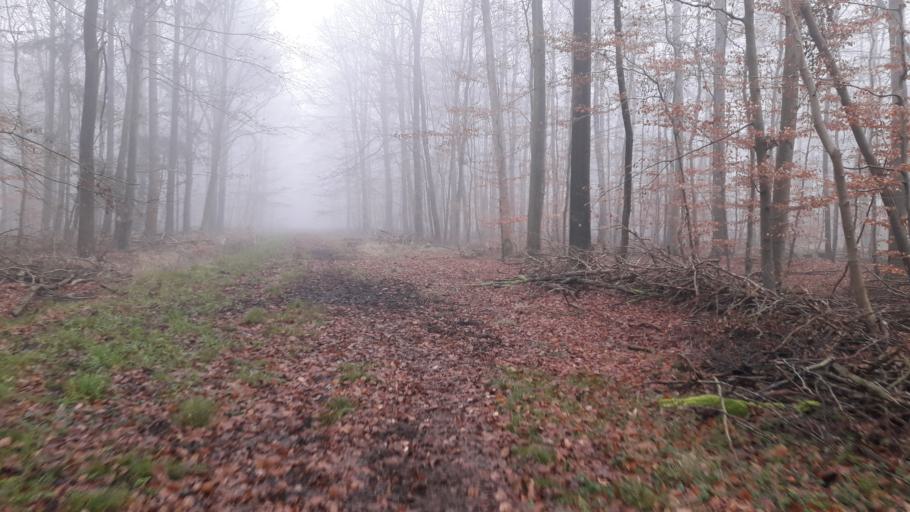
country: DE
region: Schleswig-Holstein
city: Quickborn
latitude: 53.7174
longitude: 9.8783
